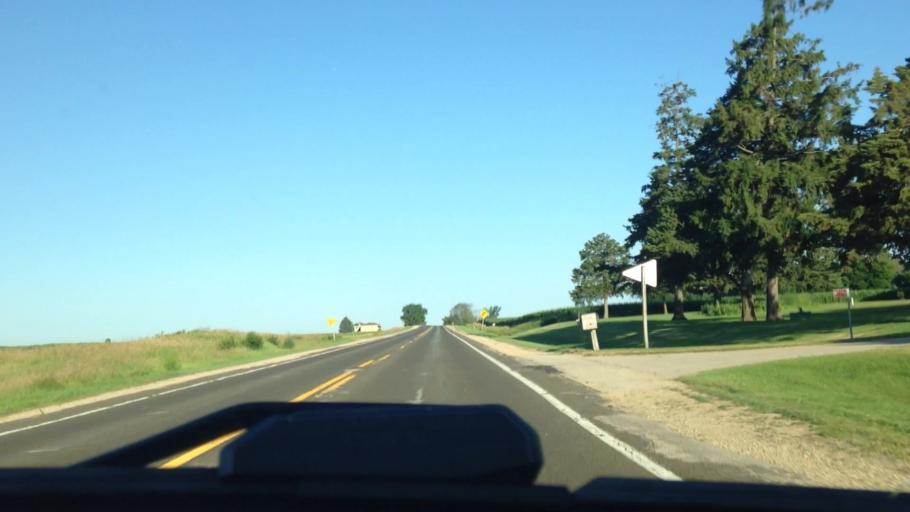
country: US
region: Wisconsin
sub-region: Columbia County
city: Poynette
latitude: 43.3322
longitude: -89.3535
